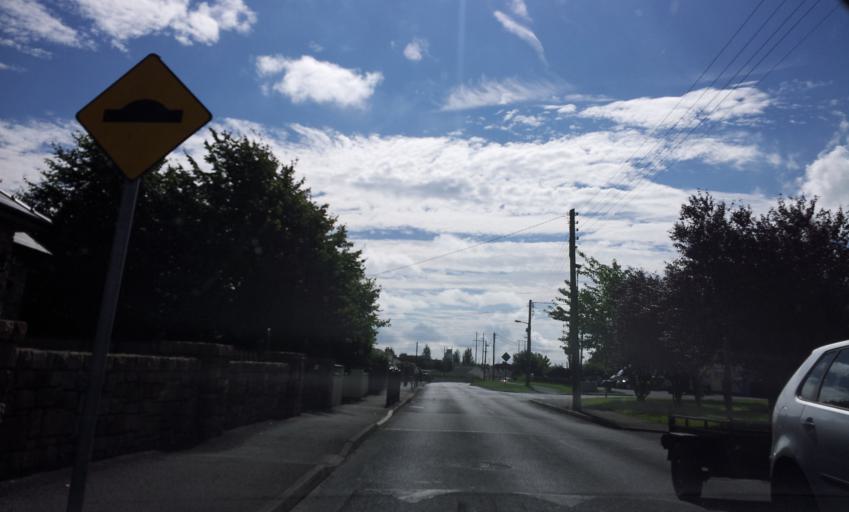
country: IE
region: Leinster
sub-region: Laois
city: Portlaoise
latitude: 53.0308
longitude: -7.2925
